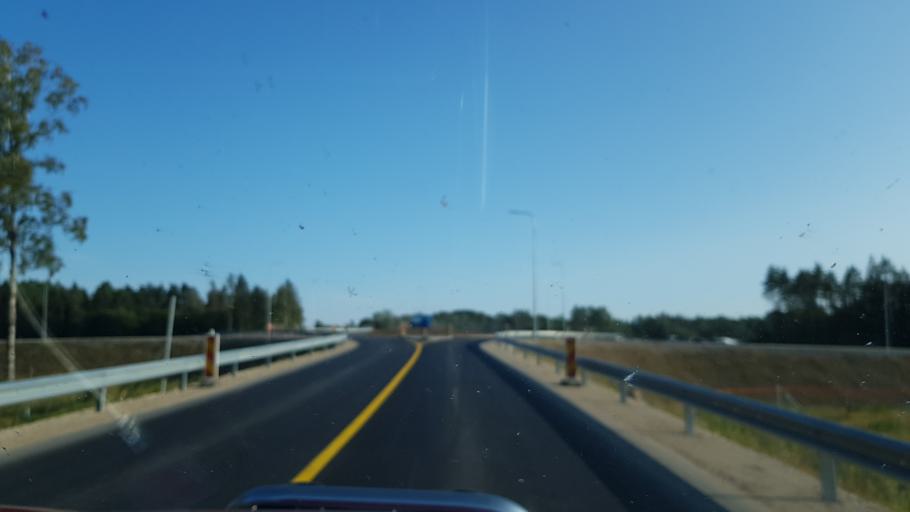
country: EE
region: Harju
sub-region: Raasiku vald
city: Raasiku
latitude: 59.1603
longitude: 25.1898
